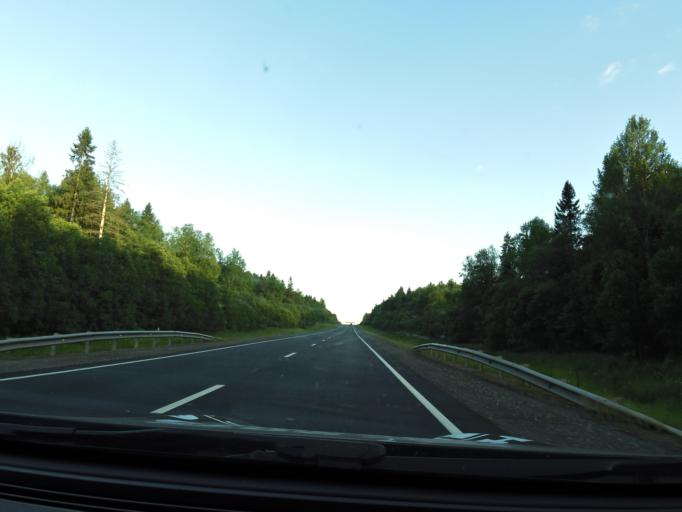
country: RU
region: Vologda
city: Gryazovets
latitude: 58.9023
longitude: 40.1830
